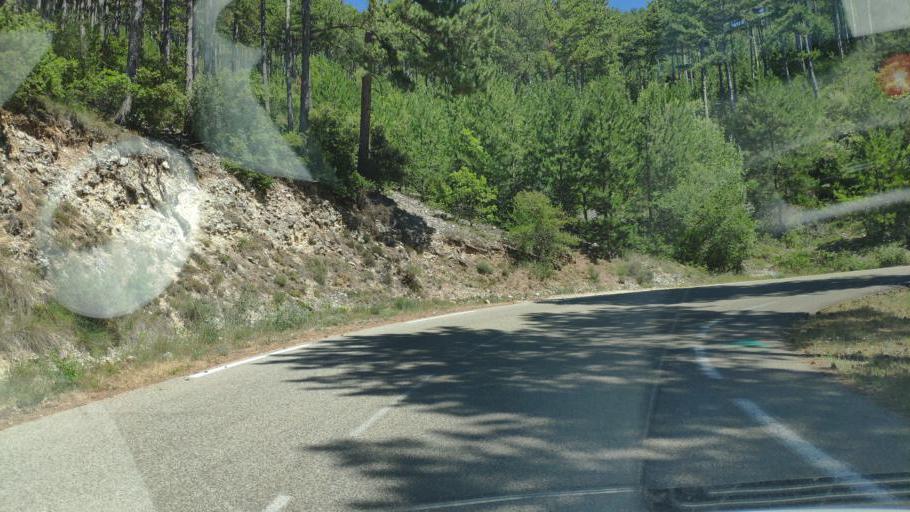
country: FR
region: Provence-Alpes-Cote d'Azur
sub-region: Departement du Vaucluse
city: Malaucene
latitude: 44.1600
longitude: 5.1489
